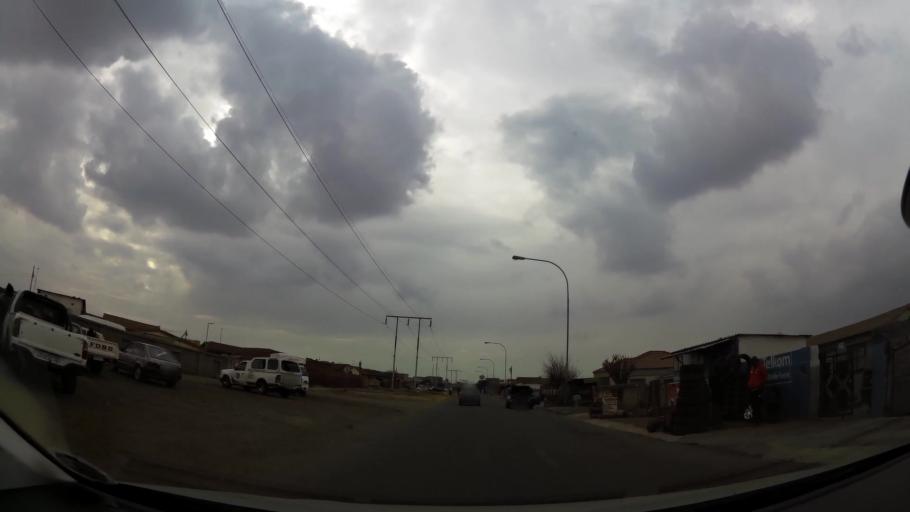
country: ZA
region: Gauteng
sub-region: City of Johannesburg Metropolitan Municipality
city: Soweto
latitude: -26.2583
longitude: 27.8600
